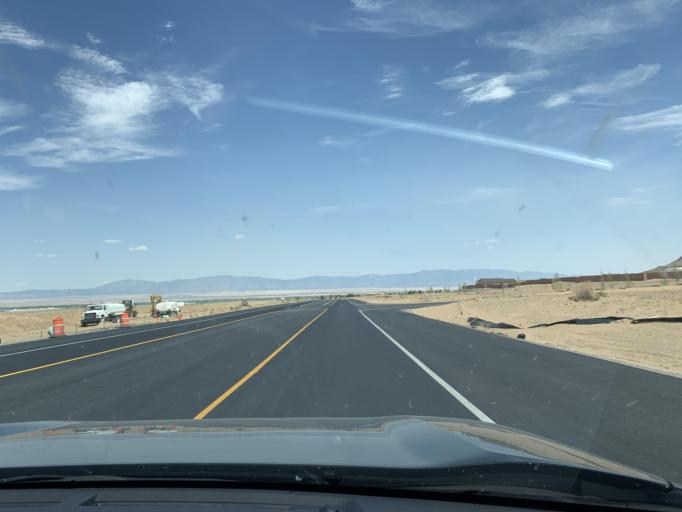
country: US
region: New Mexico
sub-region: Valencia County
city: Los Lunas
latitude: 34.8229
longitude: -106.8012
